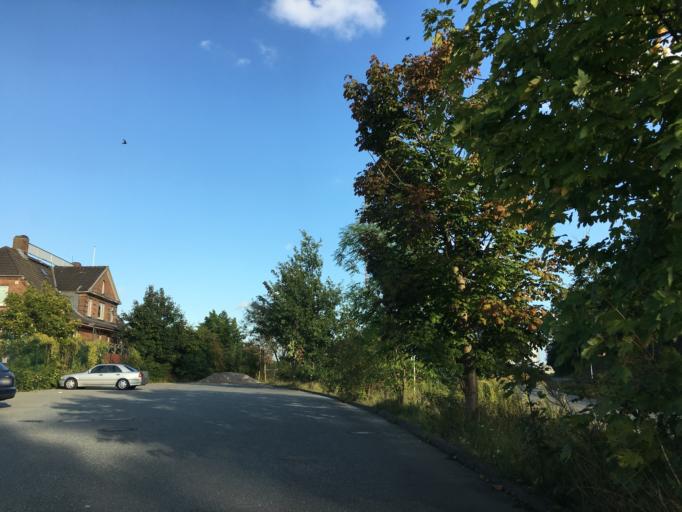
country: DE
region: Schleswig-Holstein
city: Altenholz
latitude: 54.3649
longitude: 10.1393
